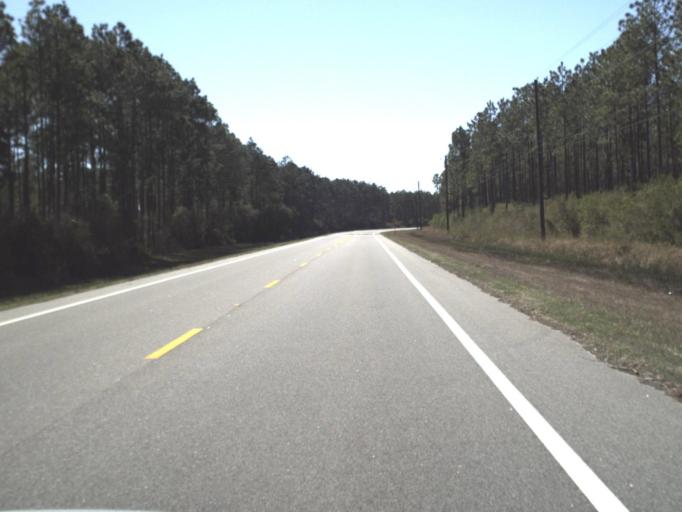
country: US
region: Florida
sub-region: Bay County
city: Laguna Beach
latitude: 30.3021
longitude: -85.8280
